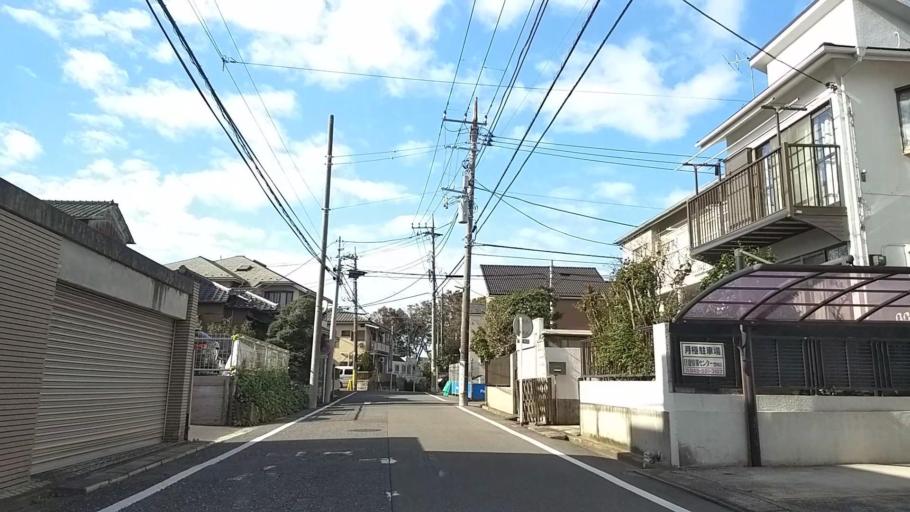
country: JP
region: Kanagawa
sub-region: Kawasaki-shi
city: Kawasaki
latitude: 35.5149
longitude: 139.6677
